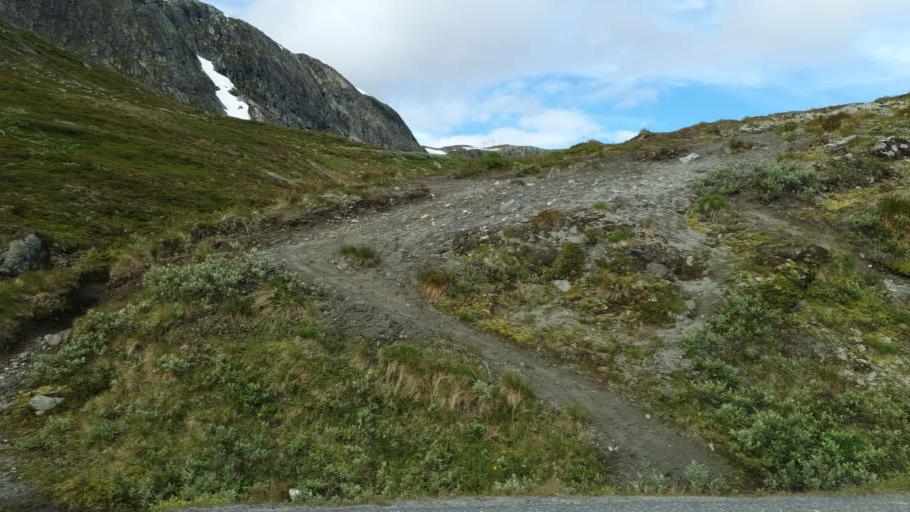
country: NO
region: Oppland
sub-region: Vestre Slidre
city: Slidre
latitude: 61.3428
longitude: 8.8125
